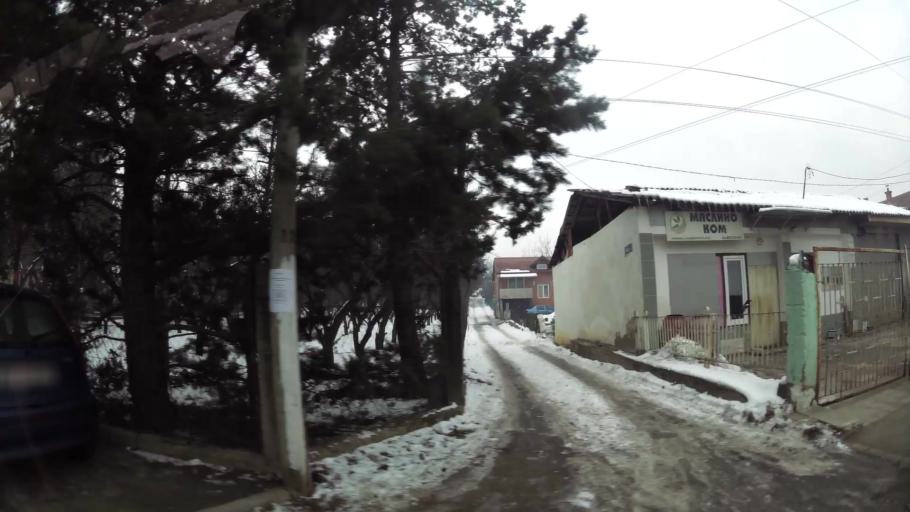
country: MK
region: Saraj
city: Saraj
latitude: 42.0379
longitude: 21.3487
